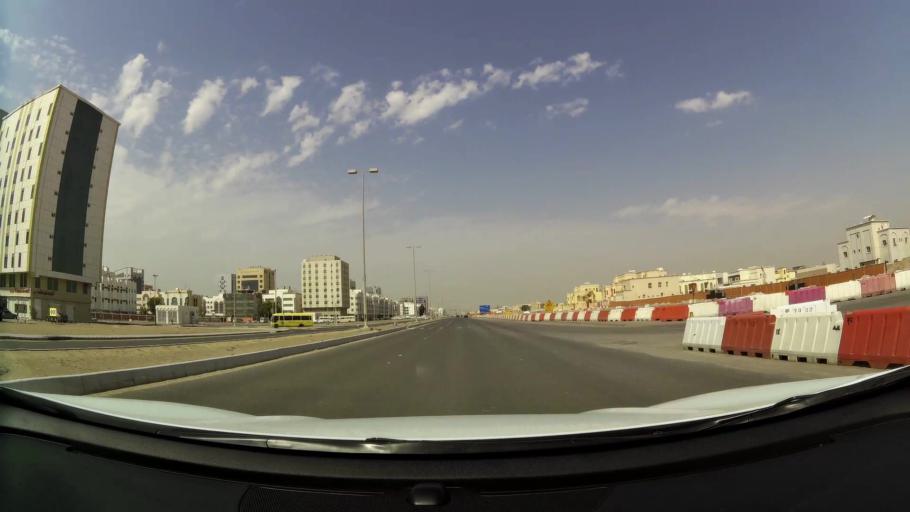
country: AE
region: Abu Dhabi
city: Abu Dhabi
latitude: 24.3202
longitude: 54.5395
